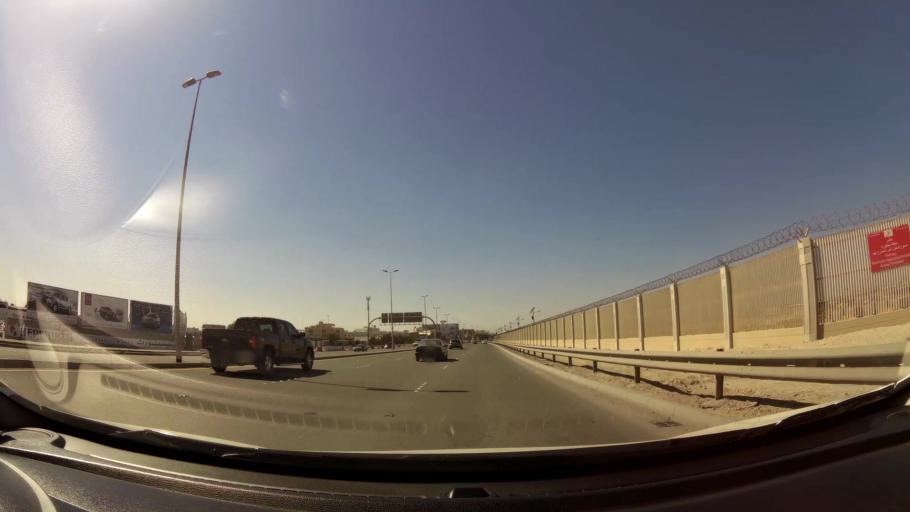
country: BH
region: Muharraq
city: Al Hadd
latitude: 26.2566
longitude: 50.6516
